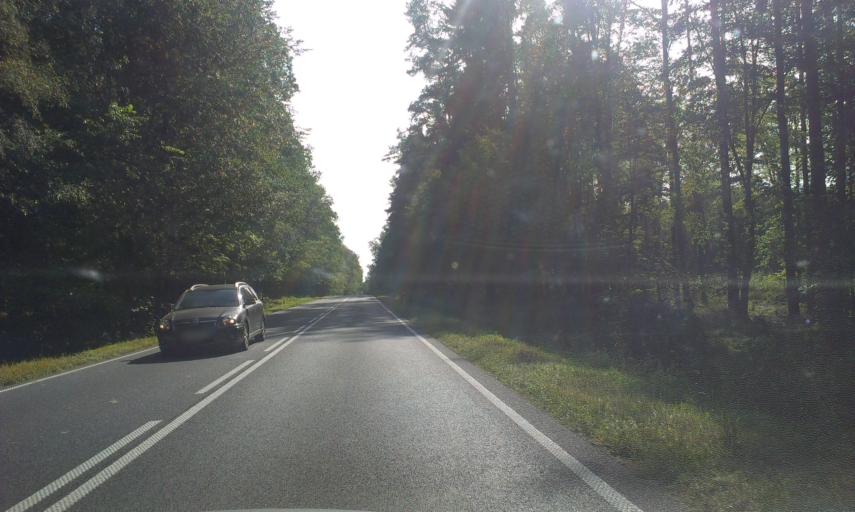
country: PL
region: West Pomeranian Voivodeship
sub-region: Powiat szczecinecki
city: Szczecinek
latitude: 53.6337
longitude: 16.7672
